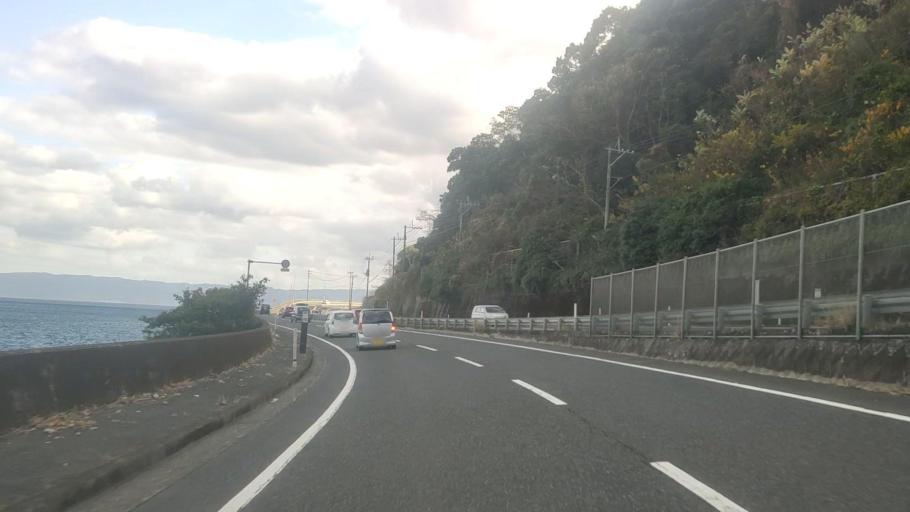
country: JP
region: Kagoshima
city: Kajiki
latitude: 31.6603
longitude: 130.6176
